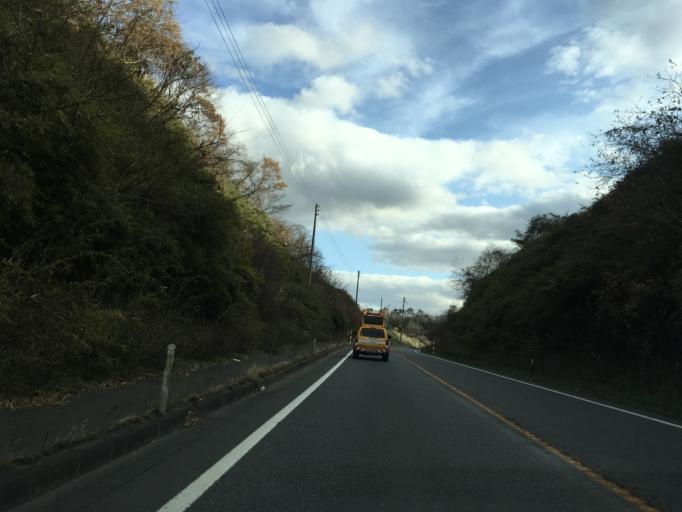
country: JP
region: Iwate
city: Ichinoseki
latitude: 38.9088
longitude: 141.1112
